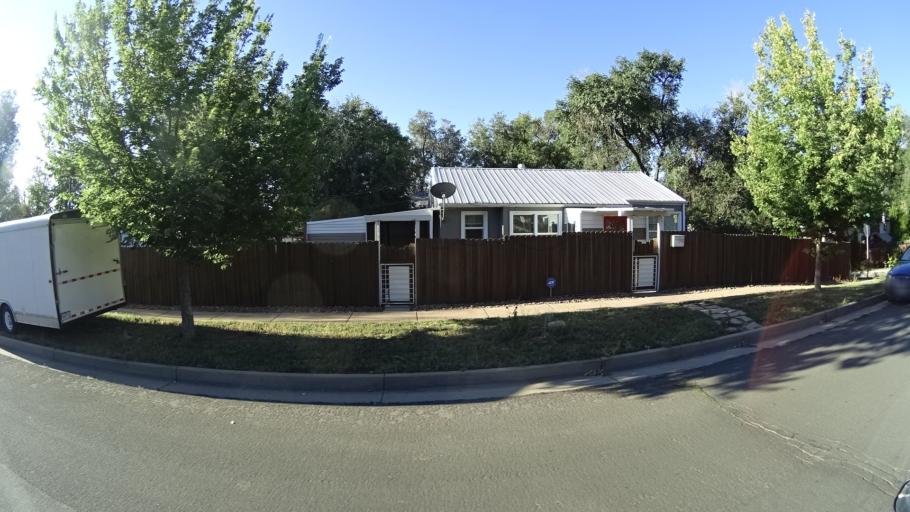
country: US
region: Colorado
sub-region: El Paso County
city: Colorado Springs
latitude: 38.8355
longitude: -104.8381
